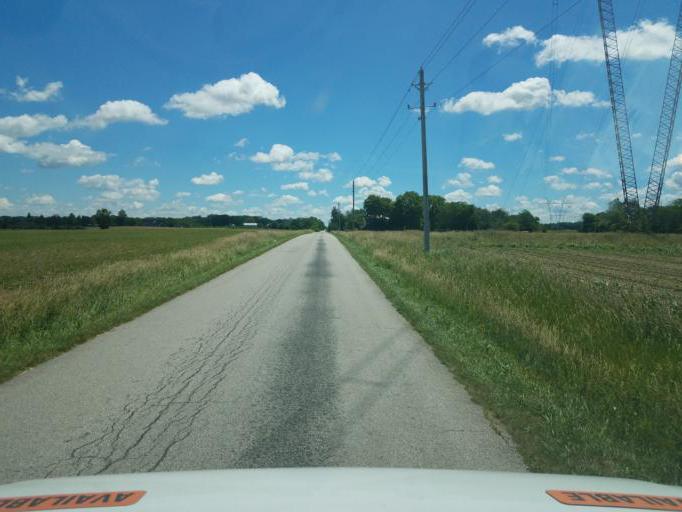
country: US
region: Ohio
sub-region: Crawford County
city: Bucyrus
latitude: 40.7401
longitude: -82.9244
